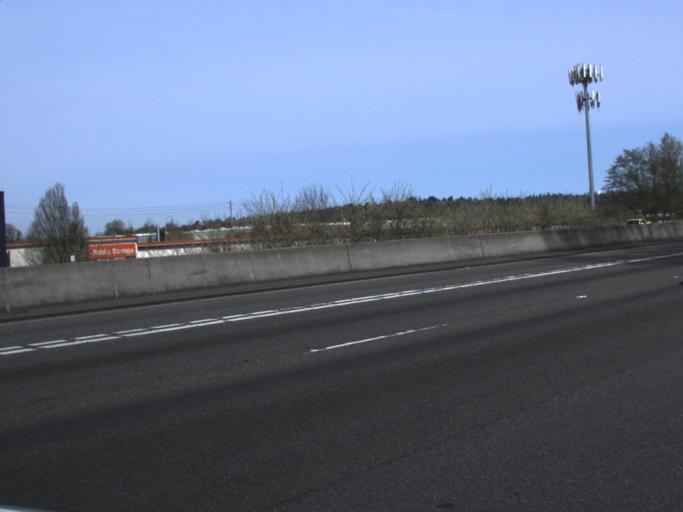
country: US
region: Washington
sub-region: Pierce County
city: Fife
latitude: 47.2394
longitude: -122.4001
